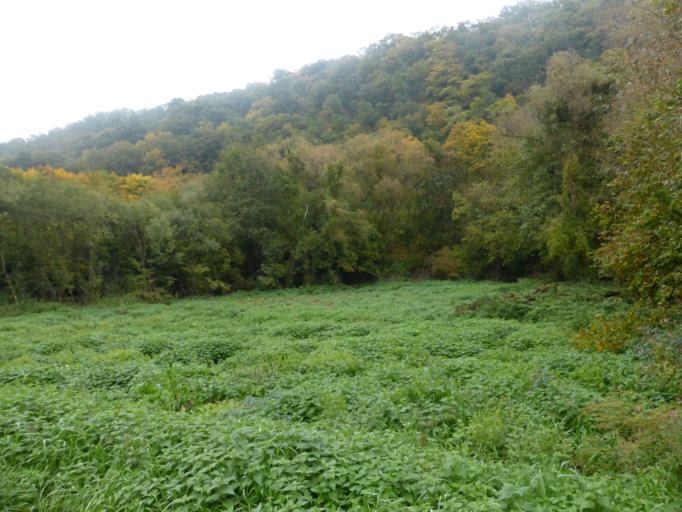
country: DE
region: Rheinland-Pfalz
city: Oberbillig
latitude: 49.7410
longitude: 6.5032
